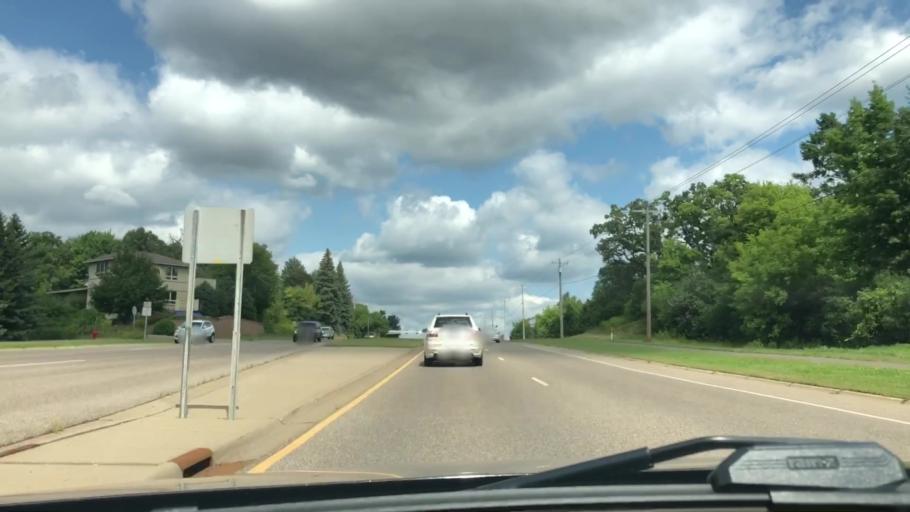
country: US
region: Minnesota
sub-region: Dakota County
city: Eagan
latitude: 44.8346
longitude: -93.1468
